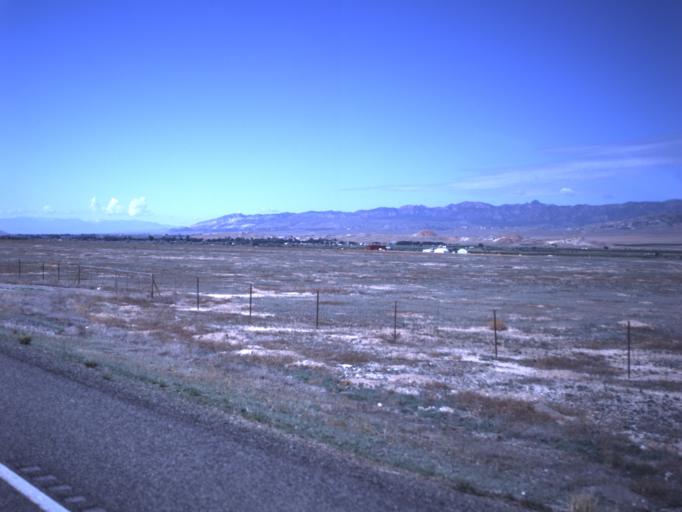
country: US
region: Utah
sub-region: Sevier County
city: Salina
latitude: 39.0360
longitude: -111.8281
